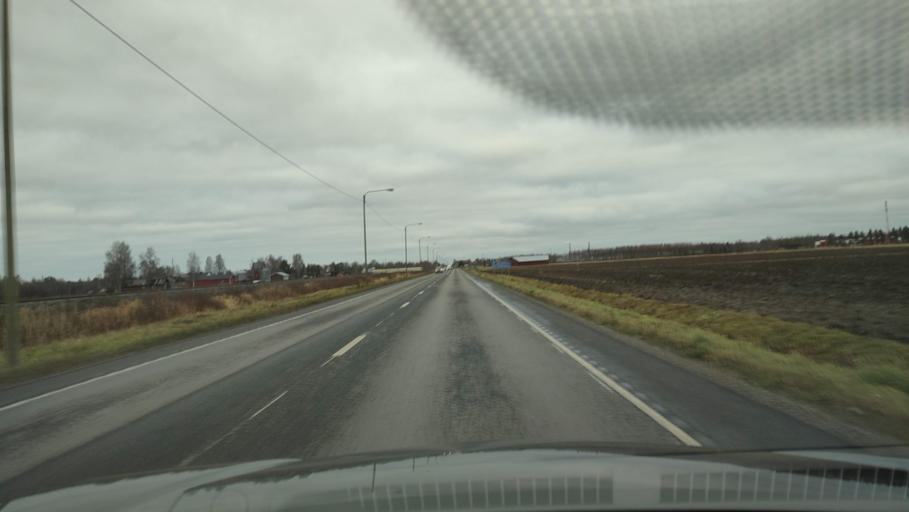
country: FI
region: Southern Ostrobothnia
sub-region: Seinaejoki
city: Ilmajoki
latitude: 62.7191
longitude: 22.5613
